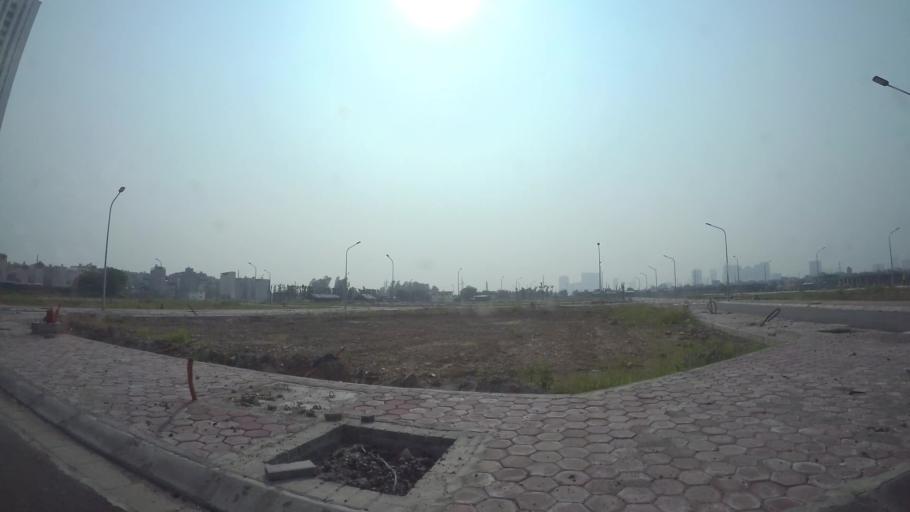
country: VN
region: Ha Noi
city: Ha Dong
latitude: 20.9528
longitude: 105.7915
